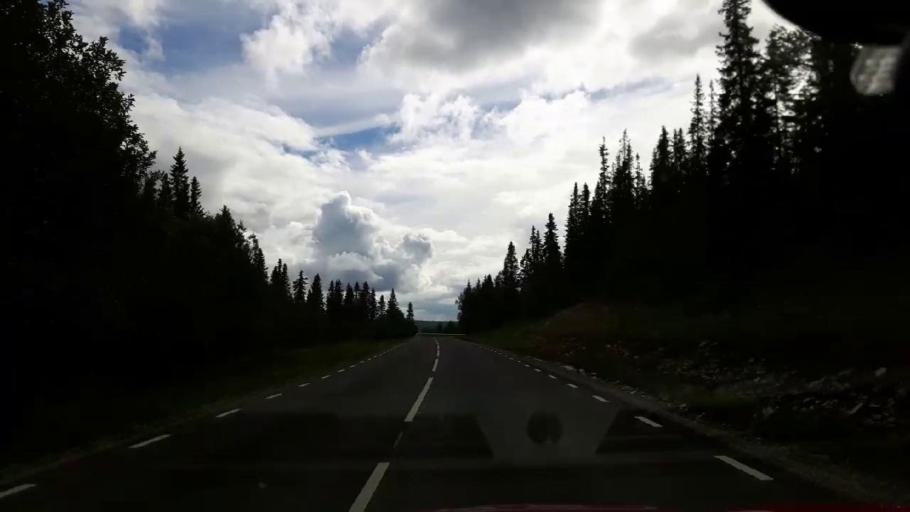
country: NO
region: Nord-Trondelag
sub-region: Royrvik
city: Royrvik
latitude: 64.8079
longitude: 14.0695
